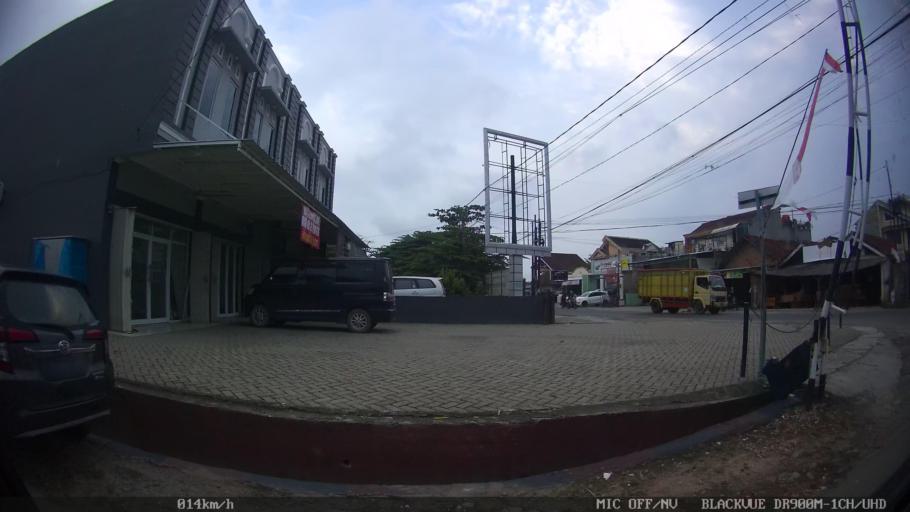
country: ID
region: Lampung
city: Kedaton
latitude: -5.4048
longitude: 105.2853
